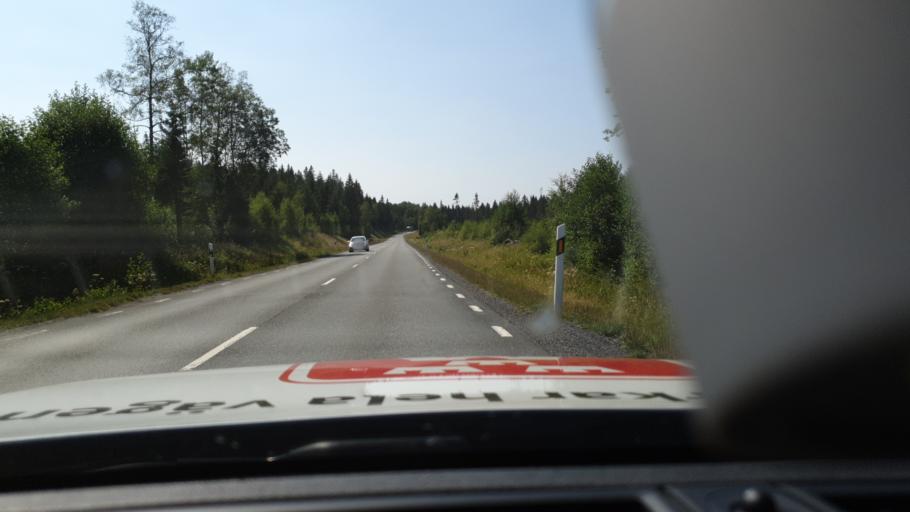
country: SE
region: Joenkoeping
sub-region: Nassjo Kommun
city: Malmback
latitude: 57.5820
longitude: 14.5016
